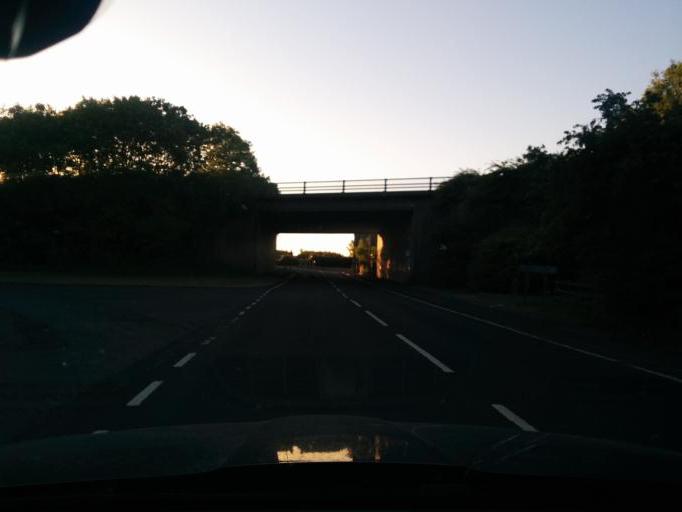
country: GB
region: England
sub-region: Northumberland
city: Cramlington
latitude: 55.1033
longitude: -1.5734
